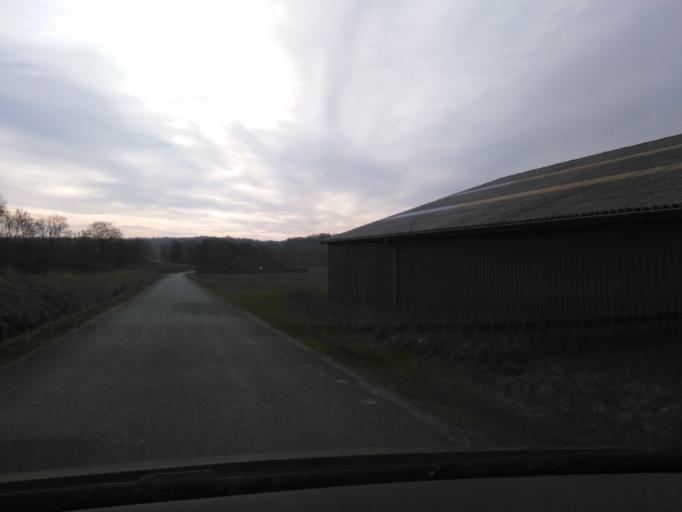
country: DK
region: Central Jutland
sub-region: Odder Kommune
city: Odder
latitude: 55.9265
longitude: 10.1131
